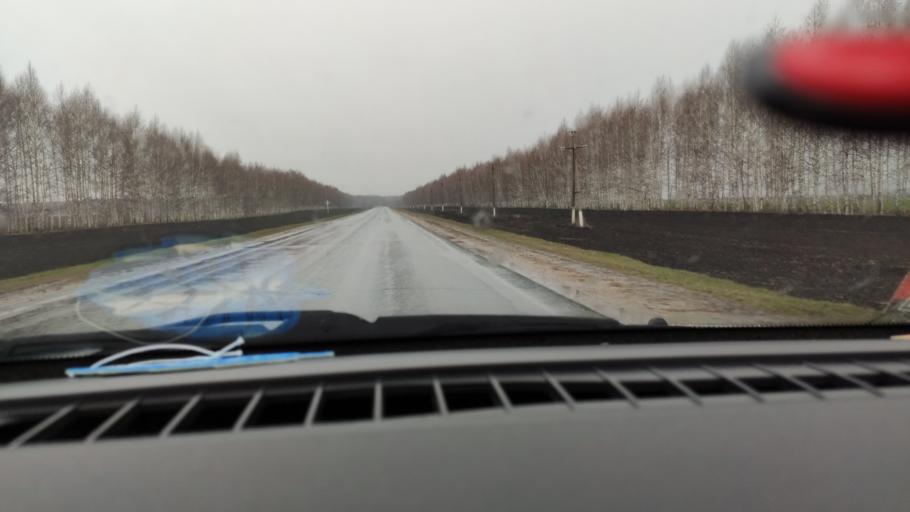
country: RU
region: Samara
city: Chelno-Vershiny
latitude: 54.6803
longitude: 51.0740
